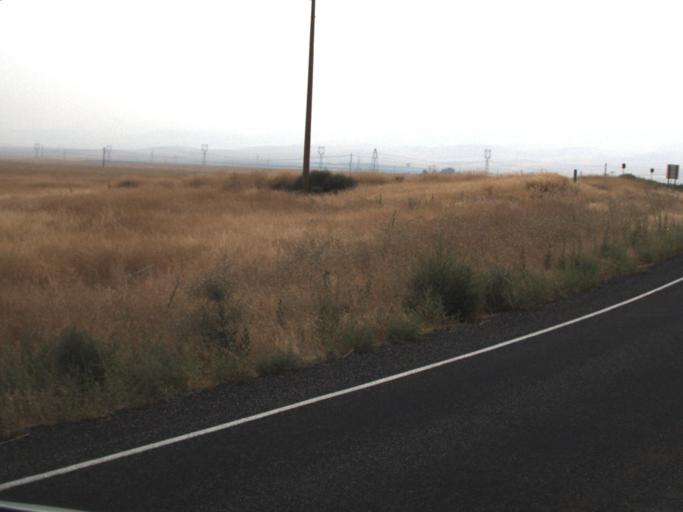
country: US
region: Washington
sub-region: Grant County
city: Desert Aire
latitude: 46.5238
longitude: -119.8745
